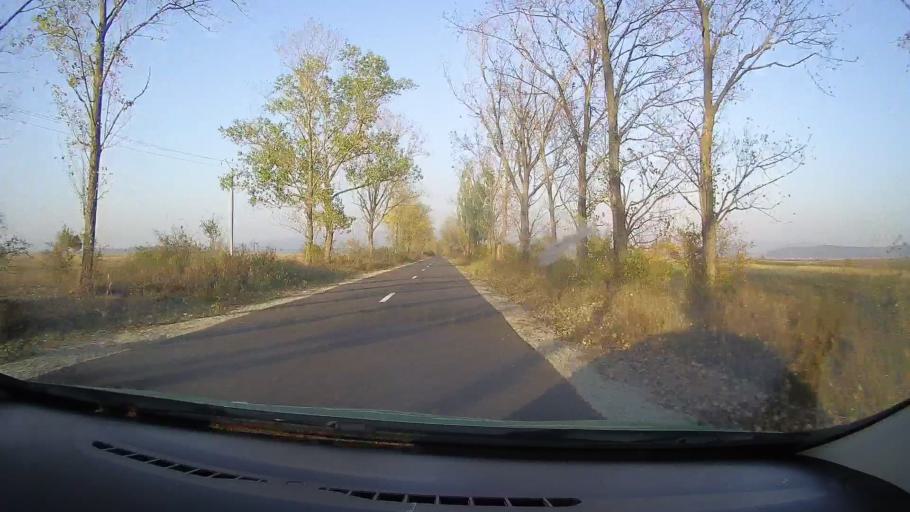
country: RO
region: Arad
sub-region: Comuna Barsa
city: Barsa
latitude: 46.3684
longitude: 22.0418
